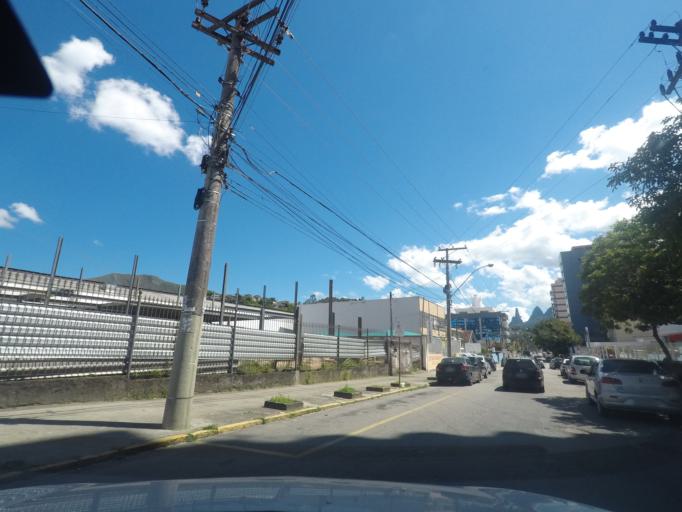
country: BR
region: Rio de Janeiro
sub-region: Teresopolis
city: Teresopolis
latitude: -22.4168
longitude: -42.9711
